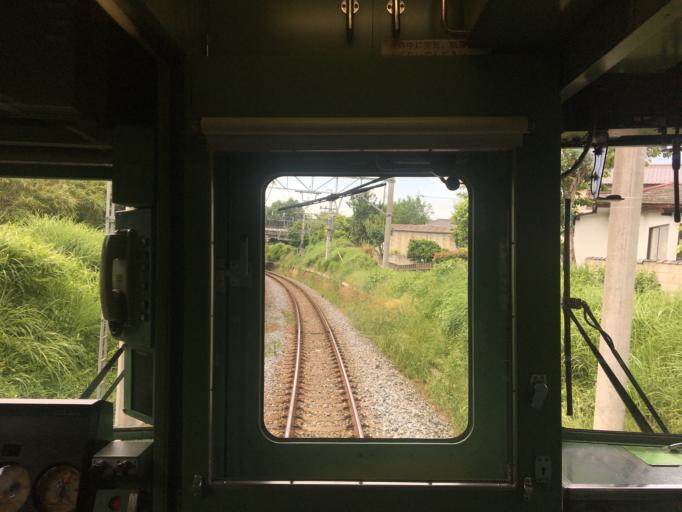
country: JP
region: Saitama
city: Yorii
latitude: 36.1108
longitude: 139.2328
